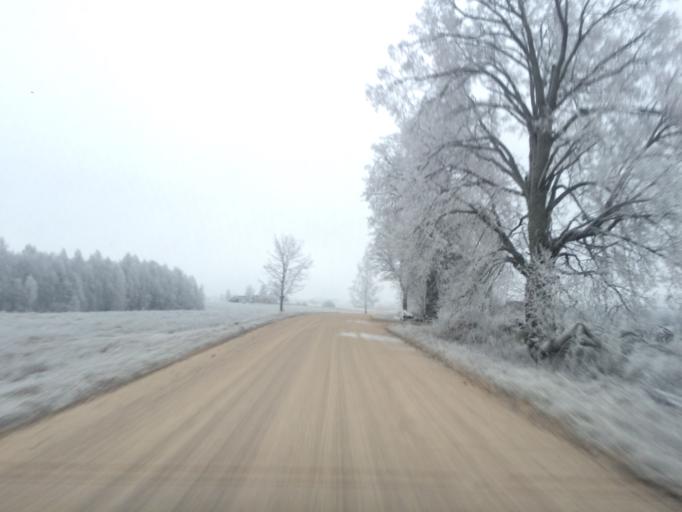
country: LV
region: Ludzas Rajons
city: Ludza
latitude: 56.6126
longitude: 27.5142
